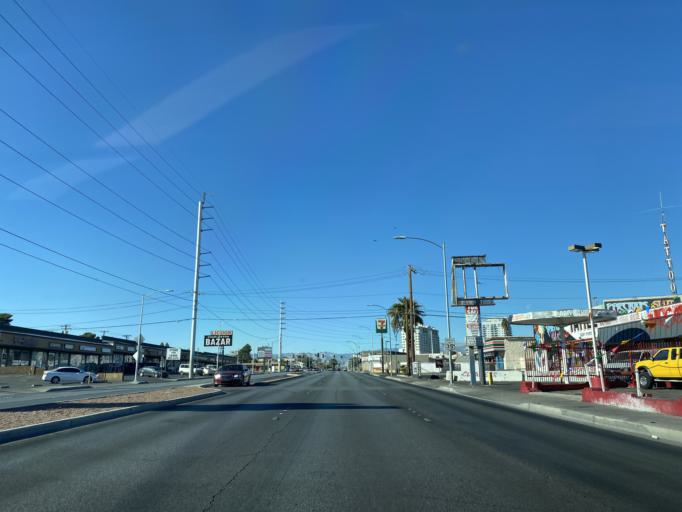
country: US
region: Nevada
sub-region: Clark County
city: Las Vegas
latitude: 36.1589
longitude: -115.1385
